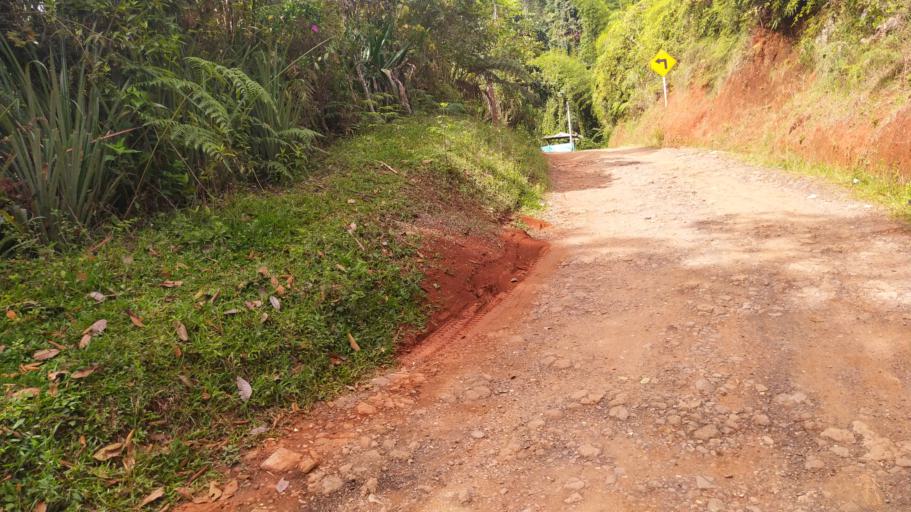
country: CO
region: Valle del Cauca
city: Cali
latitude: 3.4315
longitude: -76.6160
